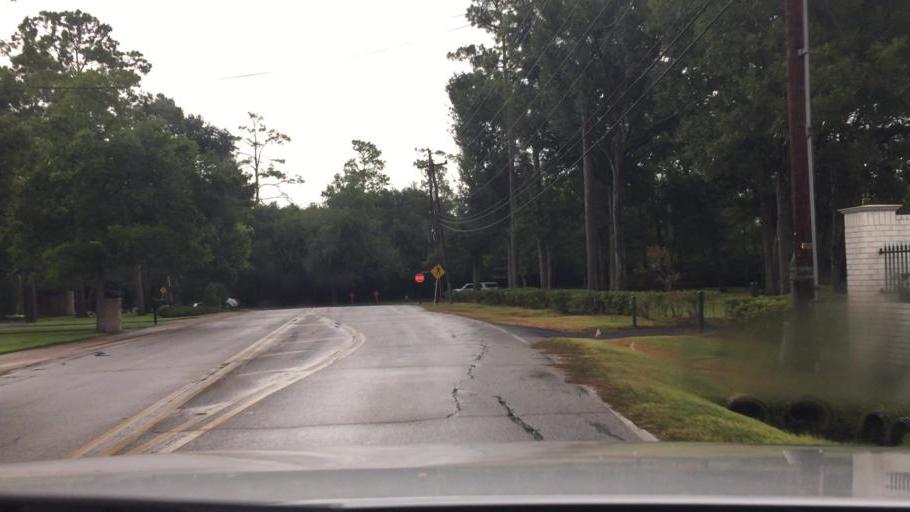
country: US
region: Texas
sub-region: Harris County
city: Hedwig Village
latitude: 29.7734
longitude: -95.5186
